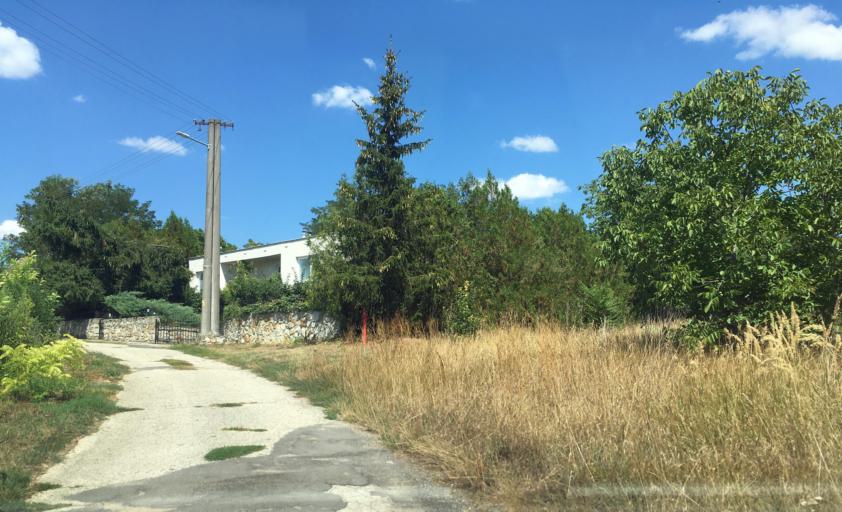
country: SK
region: Nitriansky
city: Svodin
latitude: 47.8998
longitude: 18.4252
